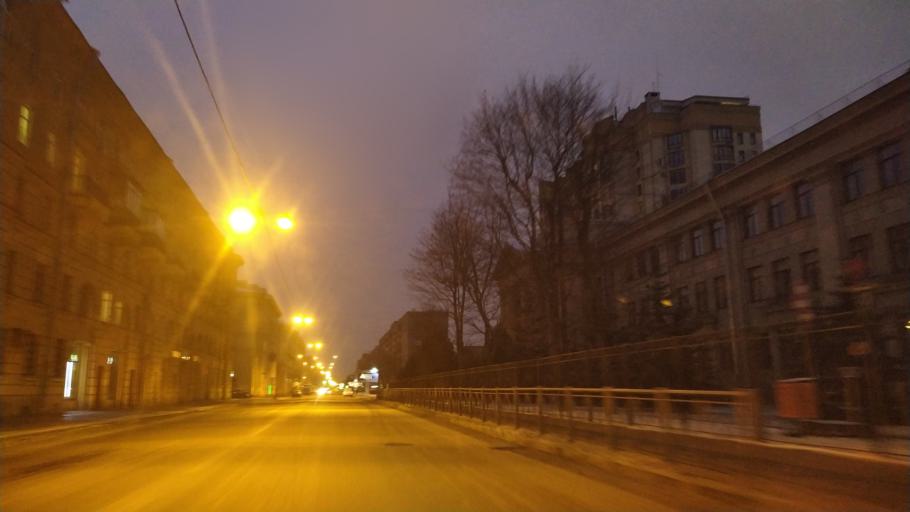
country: RU
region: Leningrad
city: Kalininskiy
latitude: 59.9573
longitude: 30.4108
